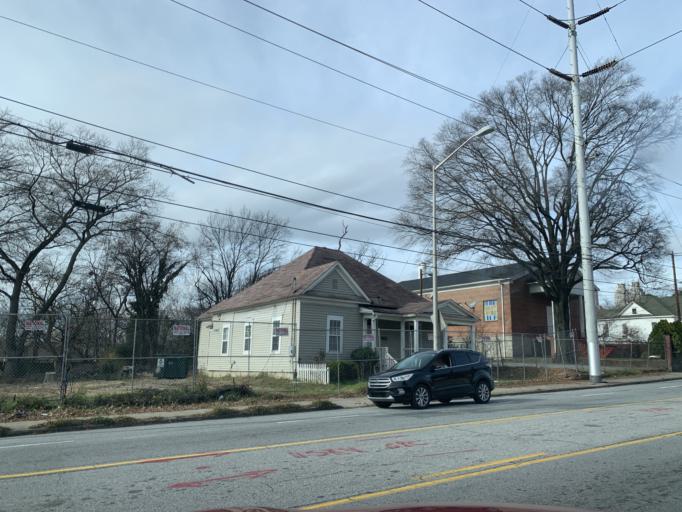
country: US
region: Georgia
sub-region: Fulton County
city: Atlanta
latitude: 33.7450
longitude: -84.3792
